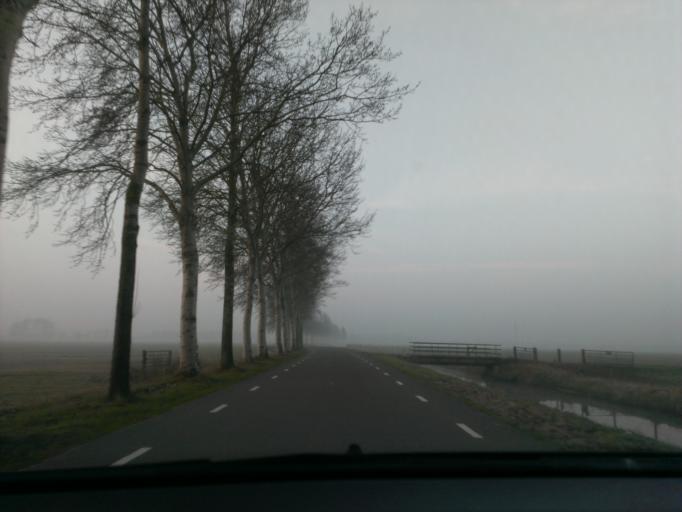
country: NL
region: Gelderland
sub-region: Gemeente Epe
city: Oene
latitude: 52.3187
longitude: 6.0481
